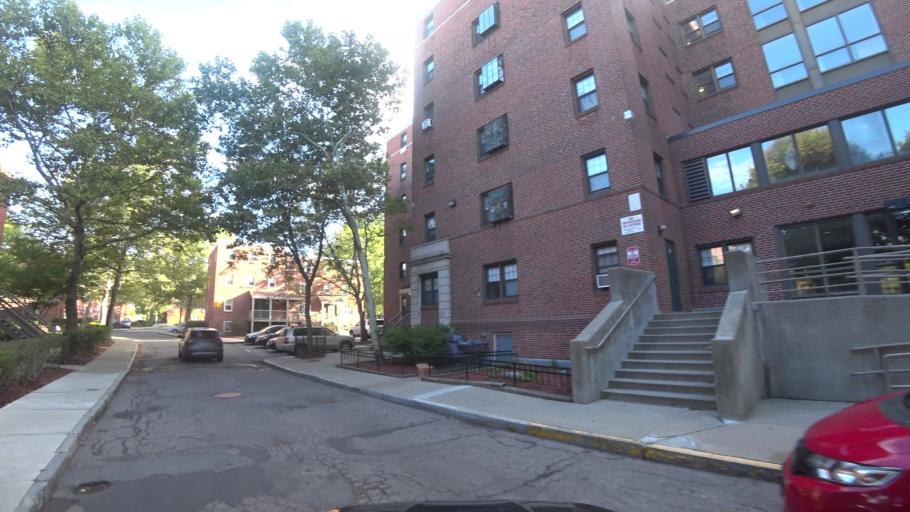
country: US
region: Massachusetts
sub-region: Middlesex County
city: Arlington
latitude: 42.3920
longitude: -71.1351
